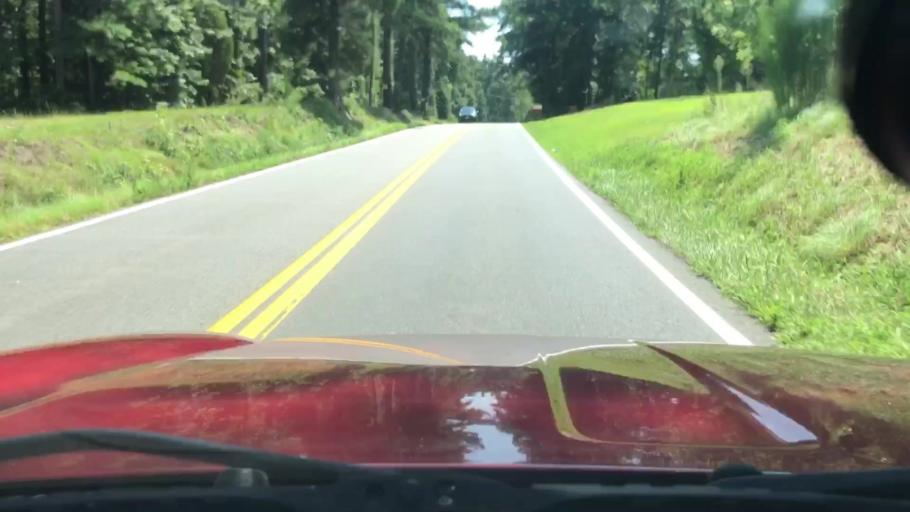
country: US
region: Virginia
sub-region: Chesterfield County
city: Chester
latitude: 37.3166
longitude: -77.4154
